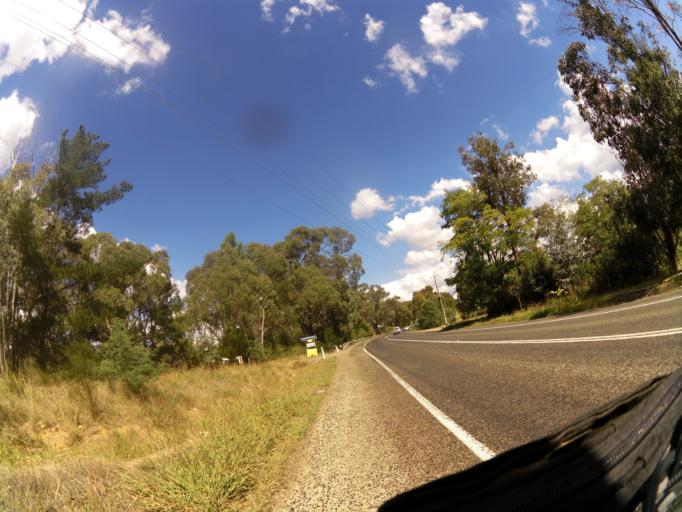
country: AU
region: Victoria
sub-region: Mansfield
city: Mansfield
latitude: -36.8291
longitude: 146.0085
